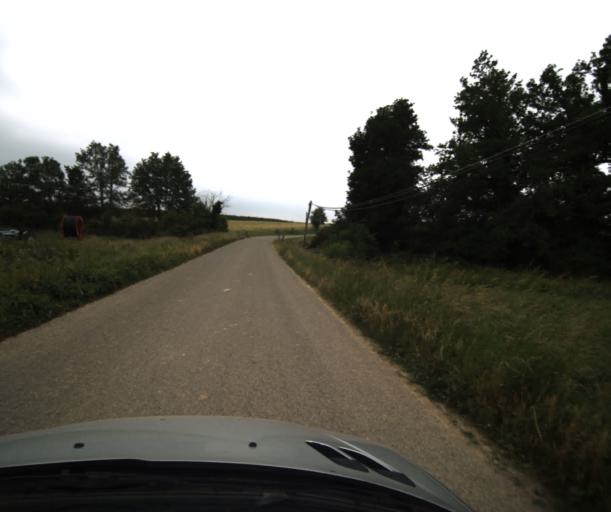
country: FR
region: Midi-Pyrenees
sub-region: Departement du Tarn-et-Garonne
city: Saint-Nicolas-de-la-Grave
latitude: 44.0573
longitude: 0.9887
